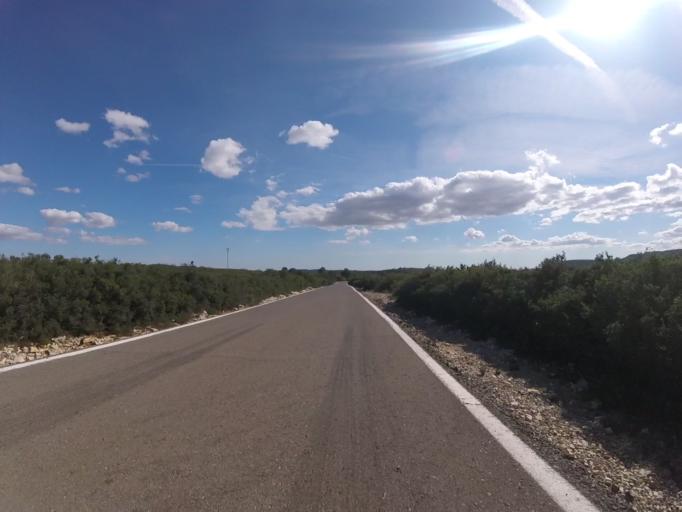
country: ES
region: Valencia
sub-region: Provincia de Castello
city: Albocasser
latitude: 40.3975
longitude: 0.0883
